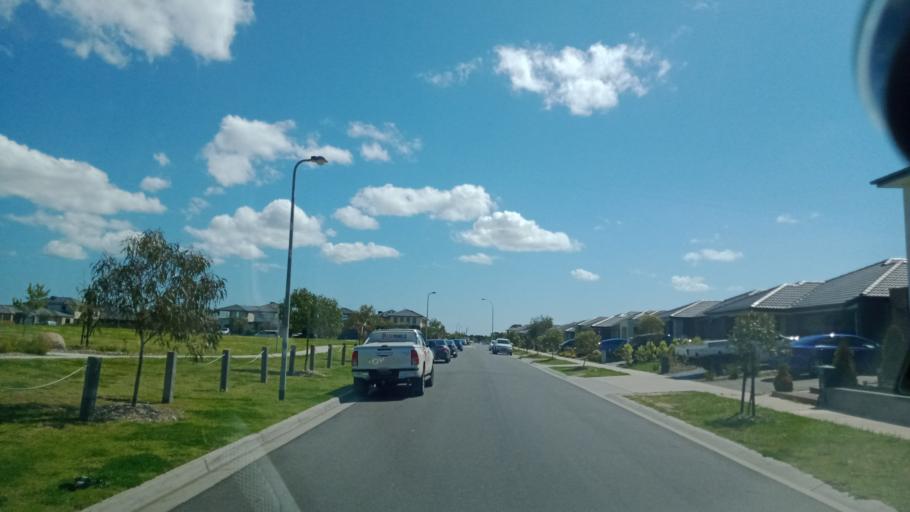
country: AU
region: Victoria
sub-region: Casey
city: Cranbourne West
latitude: -38.0991
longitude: 145.2485
